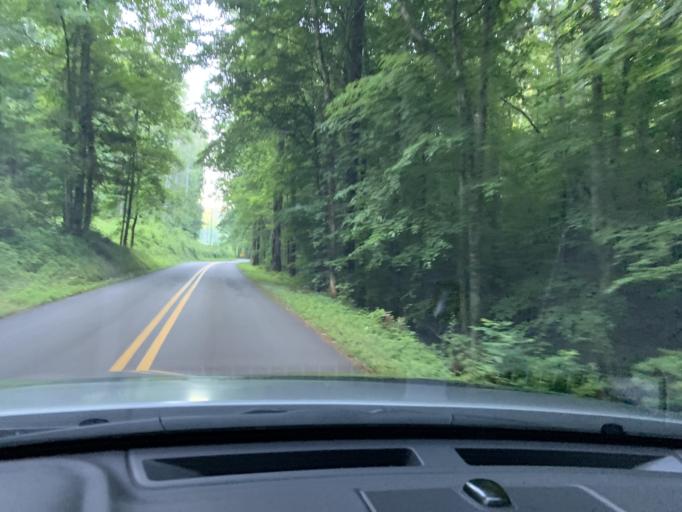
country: US
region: Georgia
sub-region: Bartow County
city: Rydal
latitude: 34.2323
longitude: -84.6617
